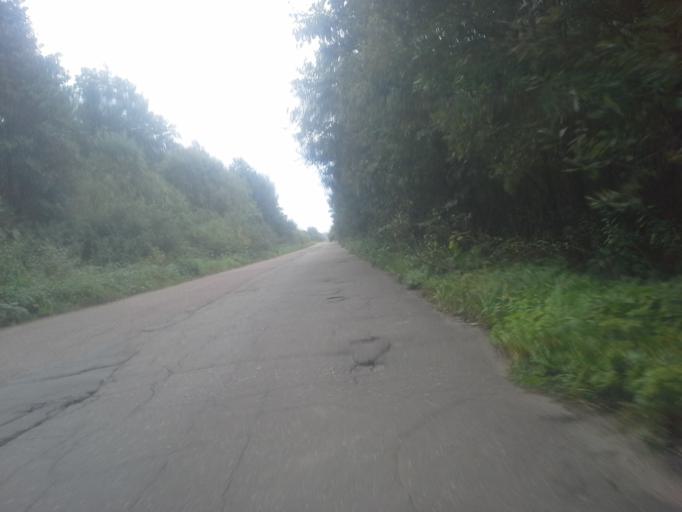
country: RU
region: Moskovskaya
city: Kievskij
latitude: 55.3849
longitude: 36.9059
